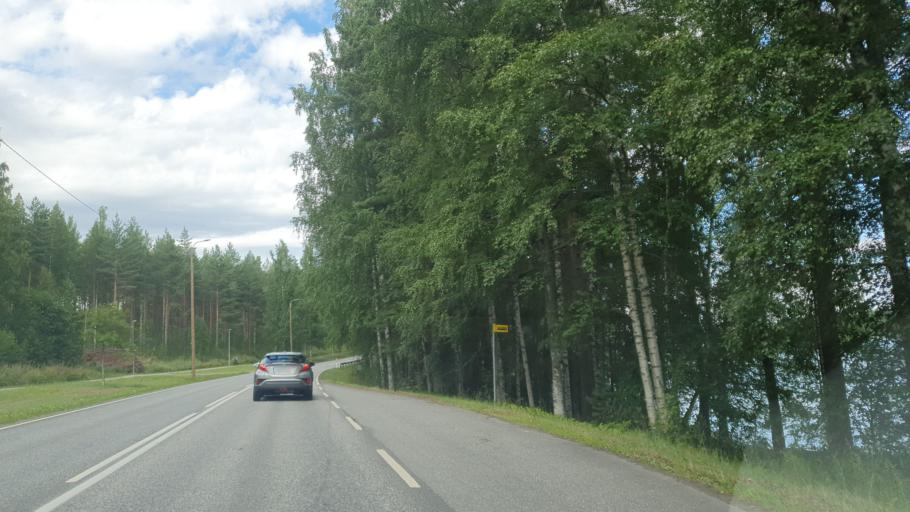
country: FI
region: Central Finland
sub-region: Jyvaeskylae
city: Saeynaetsalo
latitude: 62.1430
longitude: 25.7440
